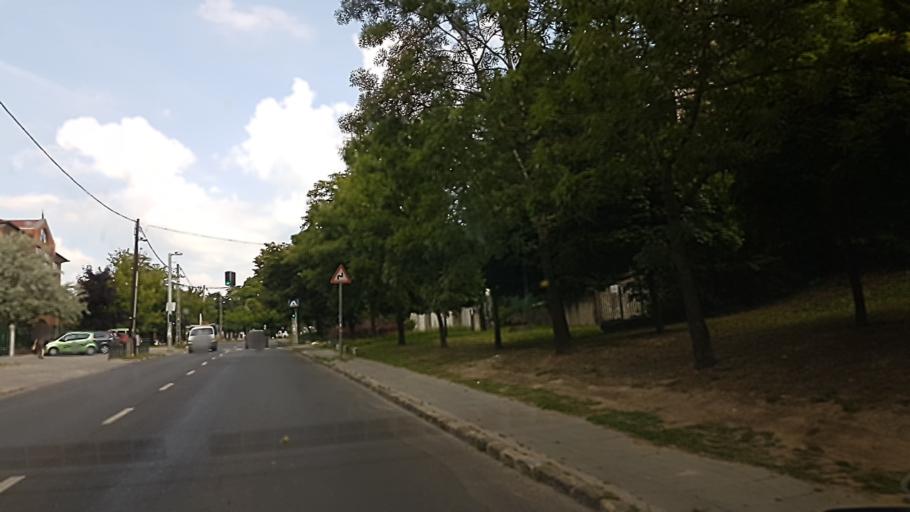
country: HU
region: Budapest
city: Budapest II. keruelet
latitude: 47.5250
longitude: 19.0110
